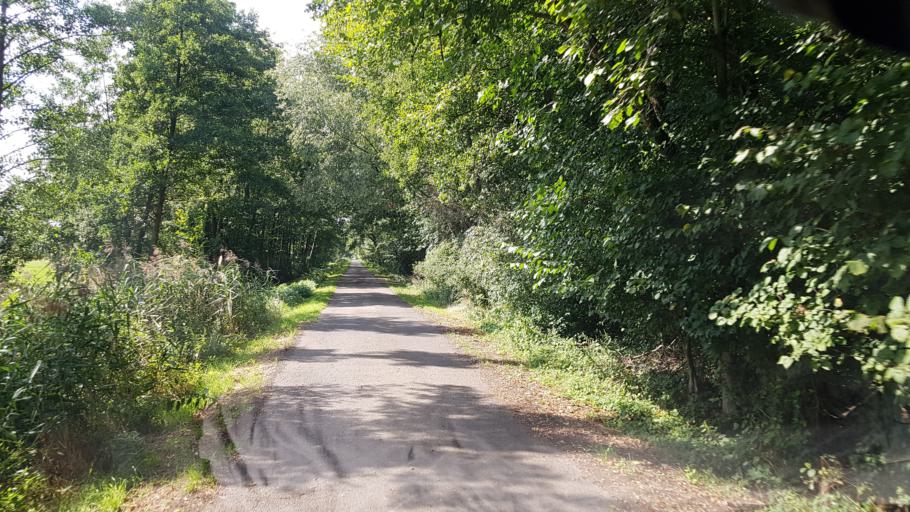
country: DE
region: Brandenburg
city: Lubbenau
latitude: 51.8912
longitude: 13.9271
